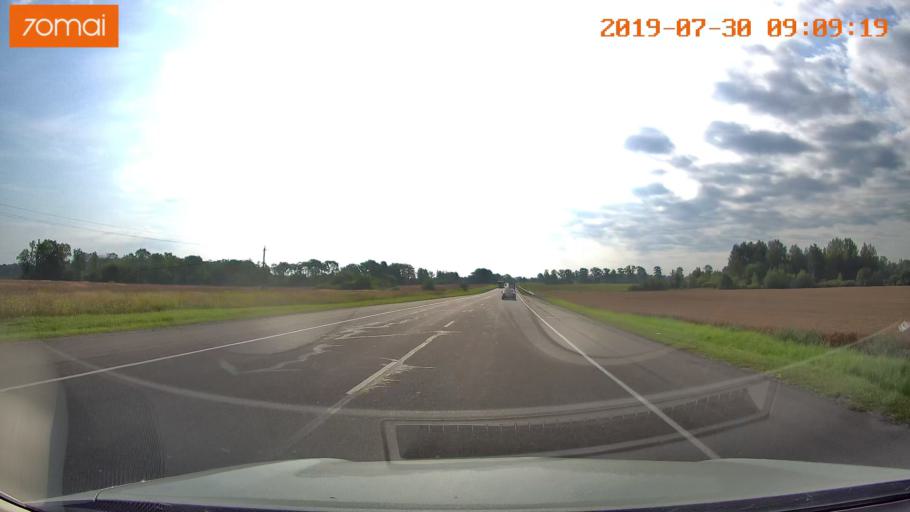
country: RU
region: Kaliningrad
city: Nesterov
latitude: 54.6138
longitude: 22.4073
